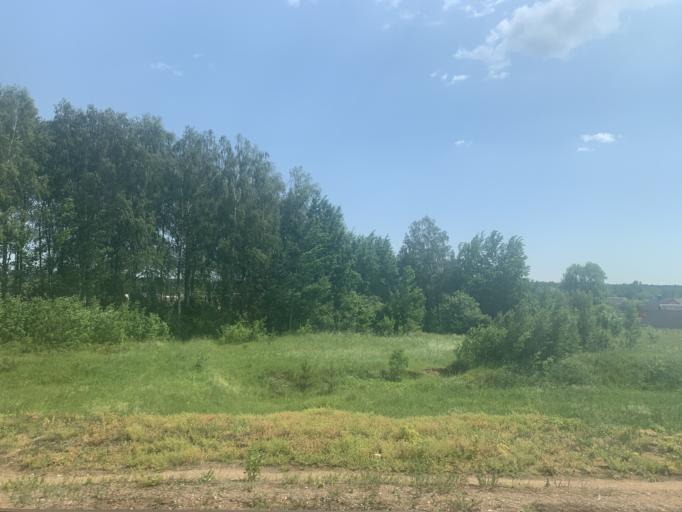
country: BY
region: Minsk
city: Stowbtsy
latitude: 53.4902
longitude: 26.7676
